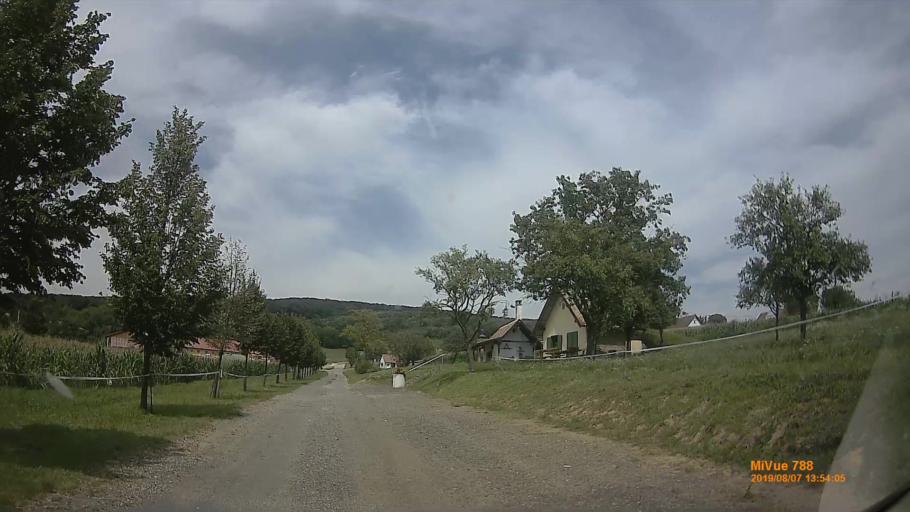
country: HU
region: Zala
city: Cserszegtomaj
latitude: 46.8942
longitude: 17.1784
